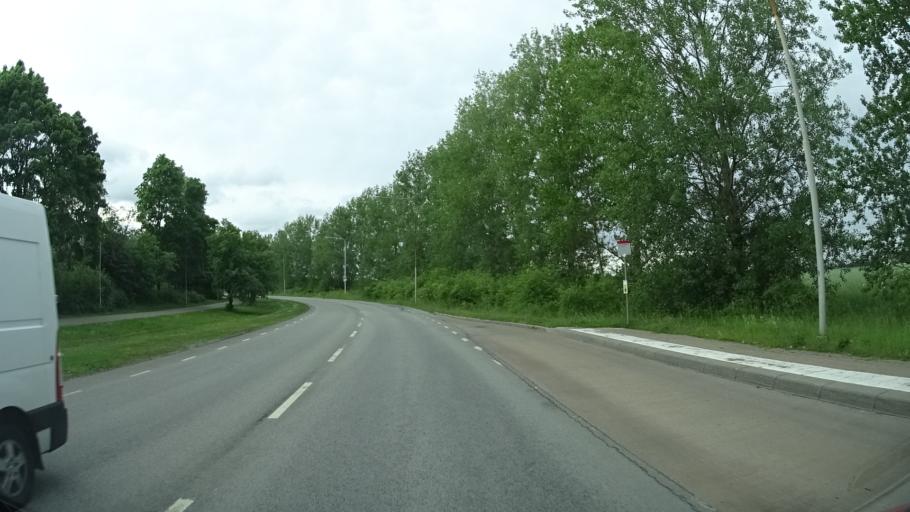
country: SE
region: OEstergoetland
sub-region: Linkopings Kommun
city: Linkoping
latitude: 58.4327
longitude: 15.5708
